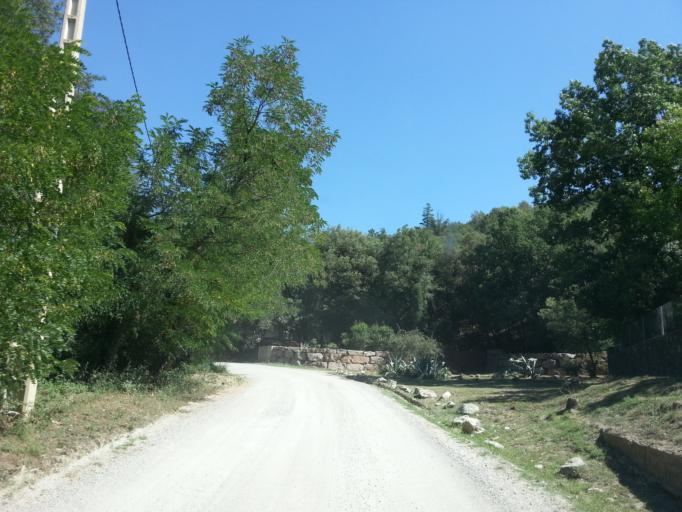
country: ES
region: Catalonia
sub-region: Provincia de Barcelona
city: Campins
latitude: 41.7366
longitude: 2.5011
